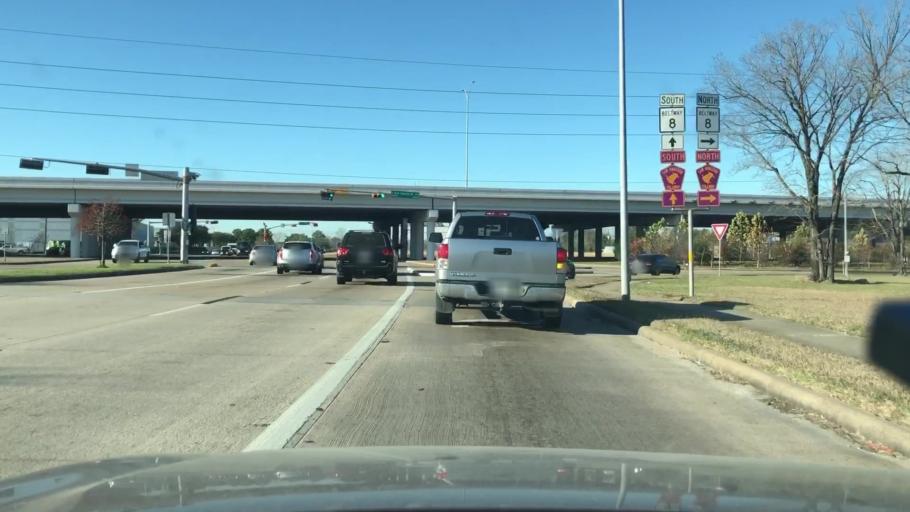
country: US
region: Texas
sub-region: Fort Bend County
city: Missouri City
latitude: 29.6449
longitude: -95.5383
